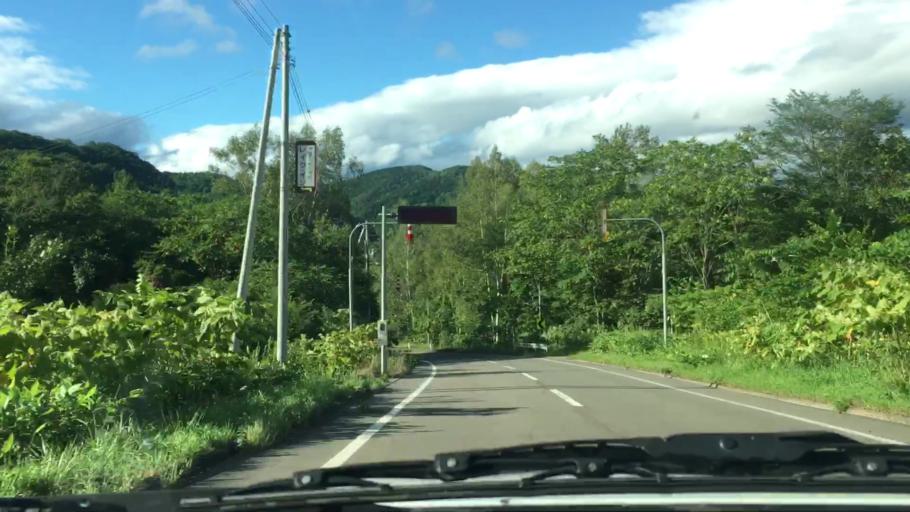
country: JP
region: Hokkaido
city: Otofuke
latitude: 43.1814
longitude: 142.9293
